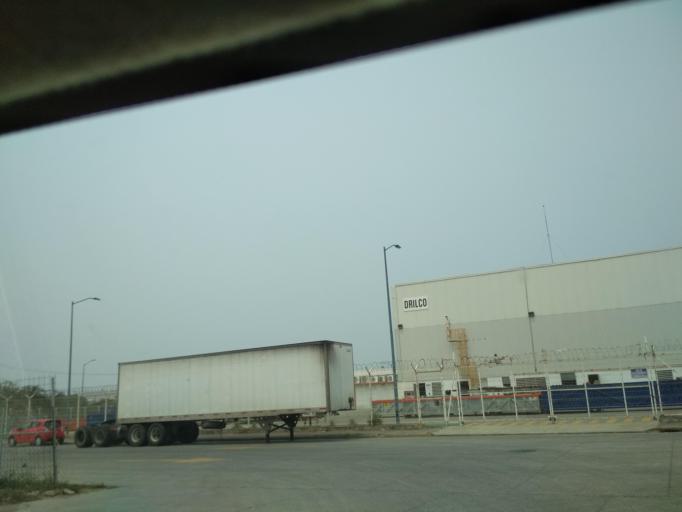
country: MX
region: Veracruz
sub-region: Veracruz
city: Las Amapolas
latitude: 19.1585
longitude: -96.2300
